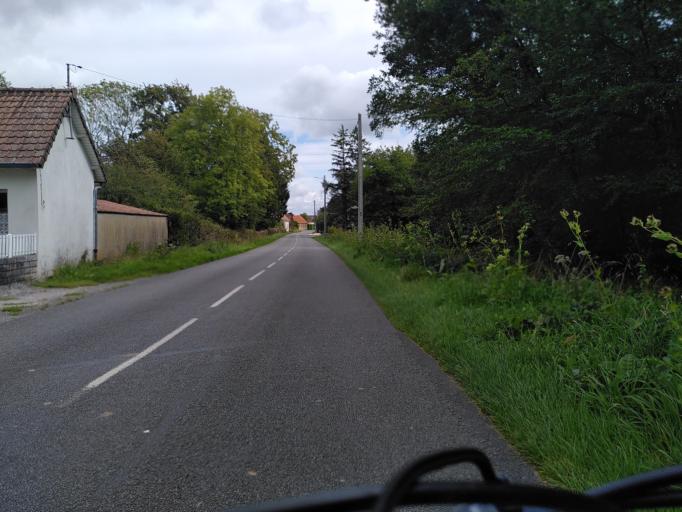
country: FR
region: Nord-Pas-de-Calais
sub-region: Departement du Pas-de-Calais
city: La Capelle-les-Boulogne
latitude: 50.7114
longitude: 1.7499
